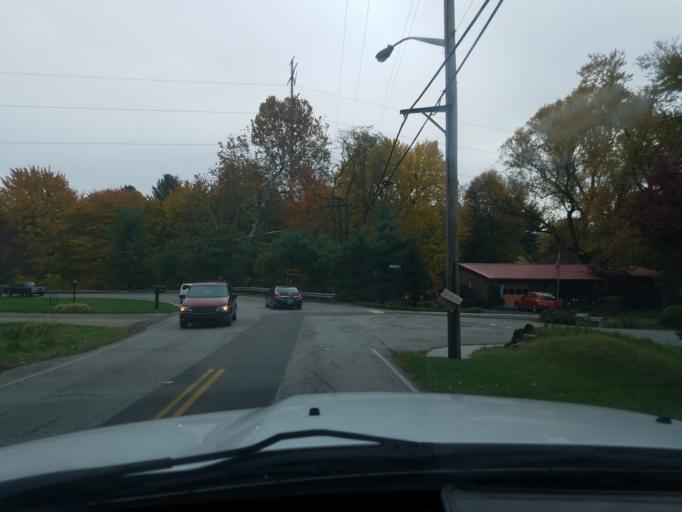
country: US
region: Indiana
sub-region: Clark County
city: Clarksville
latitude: 38.3162
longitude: -85.7772
